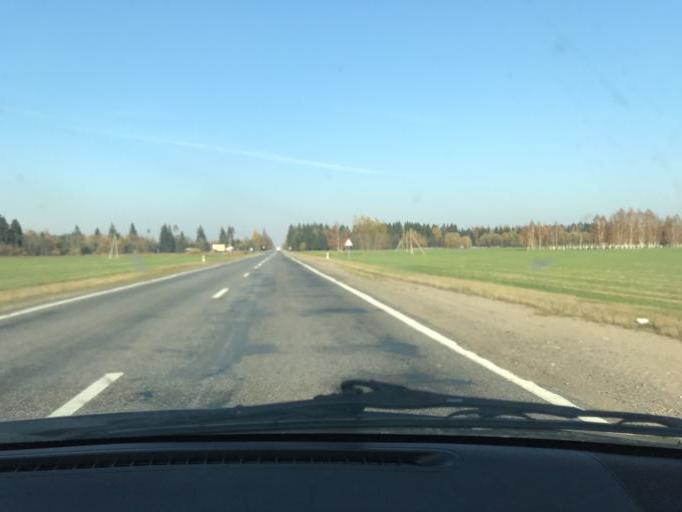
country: BY
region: Vitebsk
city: Orsha
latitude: 54.4481
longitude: 30.4900
